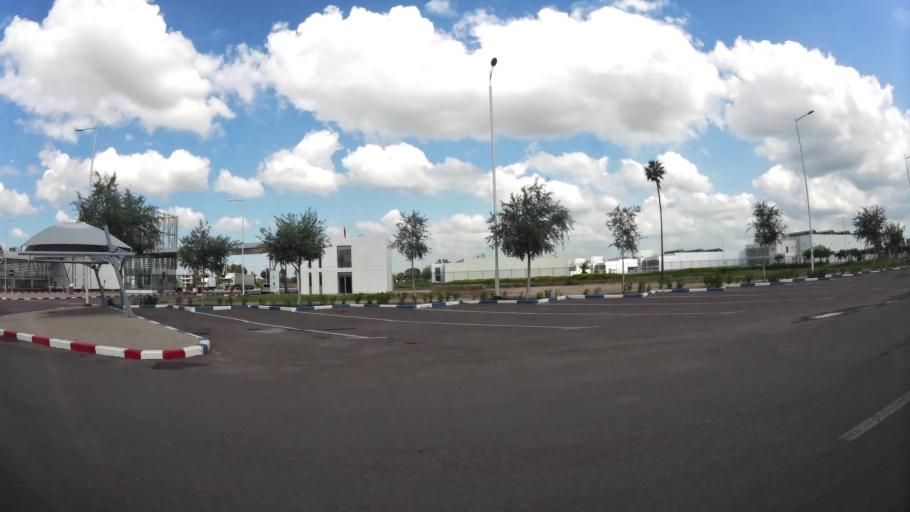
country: MA
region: Chaouia-Ouardigha
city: Nouaseur
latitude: 33.3758
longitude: -7.5679
